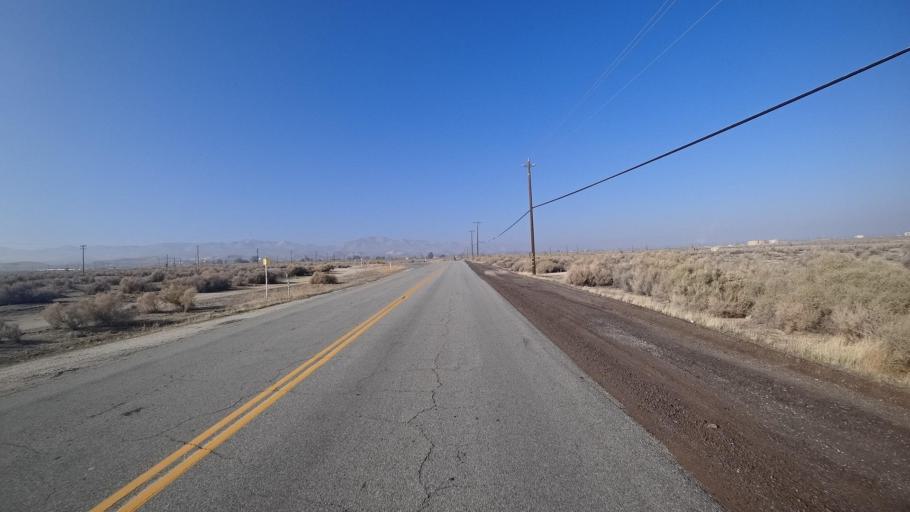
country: US
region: California
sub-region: Kern County
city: Taft Heights
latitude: 35.1801
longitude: -119.5316
